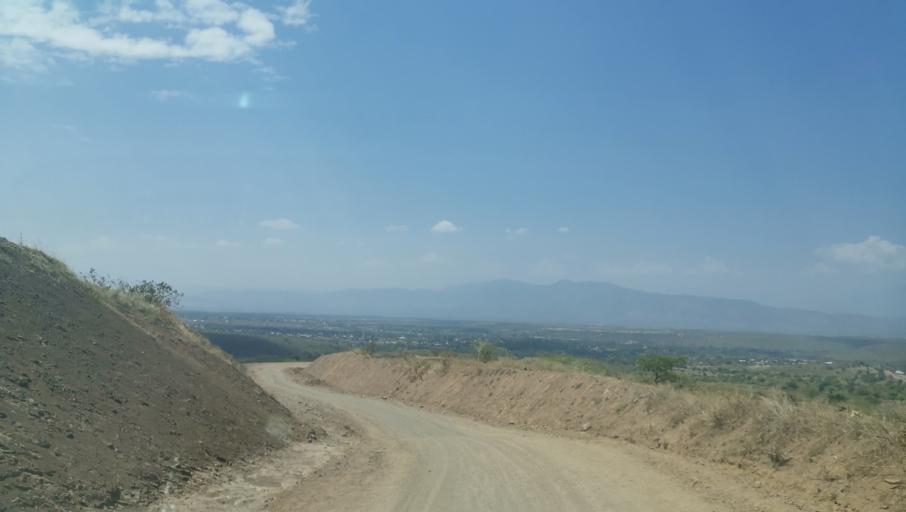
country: ET
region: Southern Nations, Nationalities, and People's Region
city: Arba Minch'
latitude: 6.3346
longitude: 37.3310
